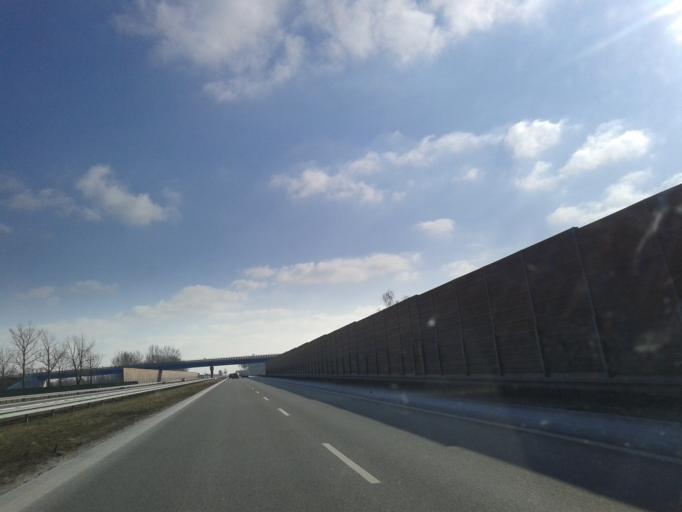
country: PL
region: Kujawsko-Pomorskie
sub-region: Powiat aleksandrowski
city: Raciazek
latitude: 52.8107
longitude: 18.8131
